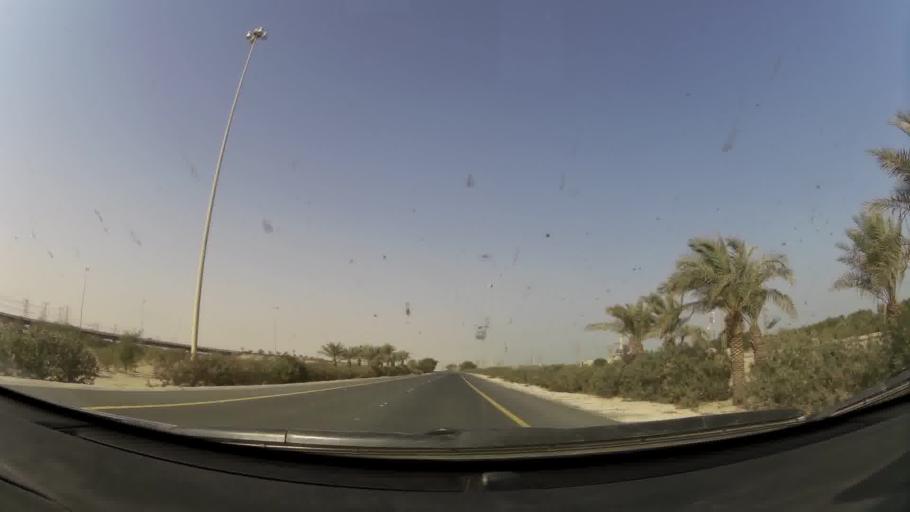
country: KW
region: Al Ahmadi
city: Al Fahahil
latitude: 28.9189
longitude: 48.2074
